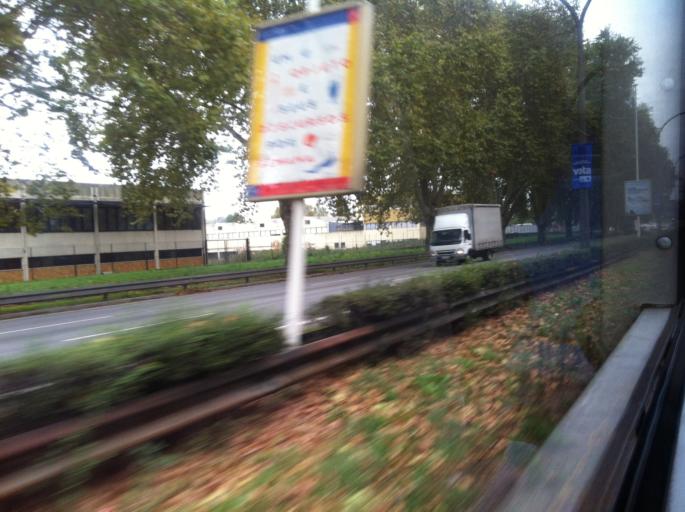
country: PT
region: Porto
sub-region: Matosinhos
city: Senhora da Hora
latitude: 41.1715
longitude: -8.6473
